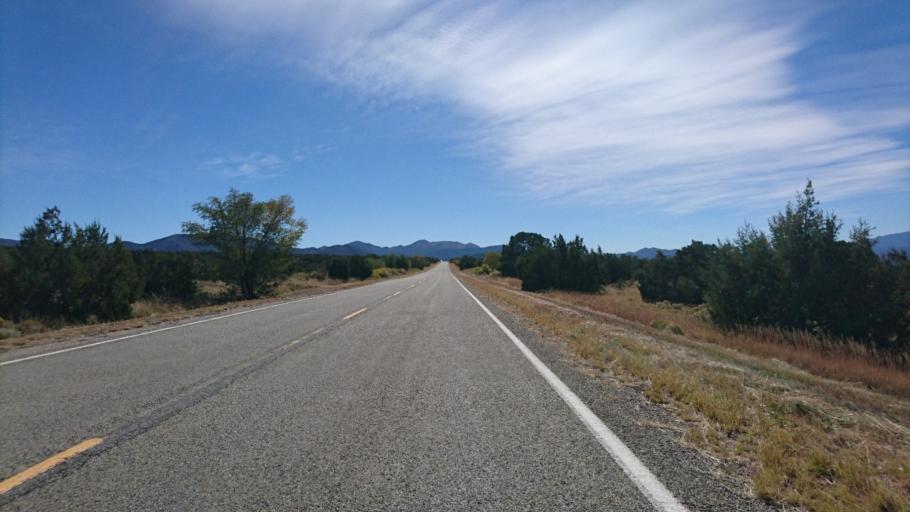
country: US
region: New Mexico
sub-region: Bernalillo County
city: Sandia Knolls
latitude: 35.3121
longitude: -106.2153
